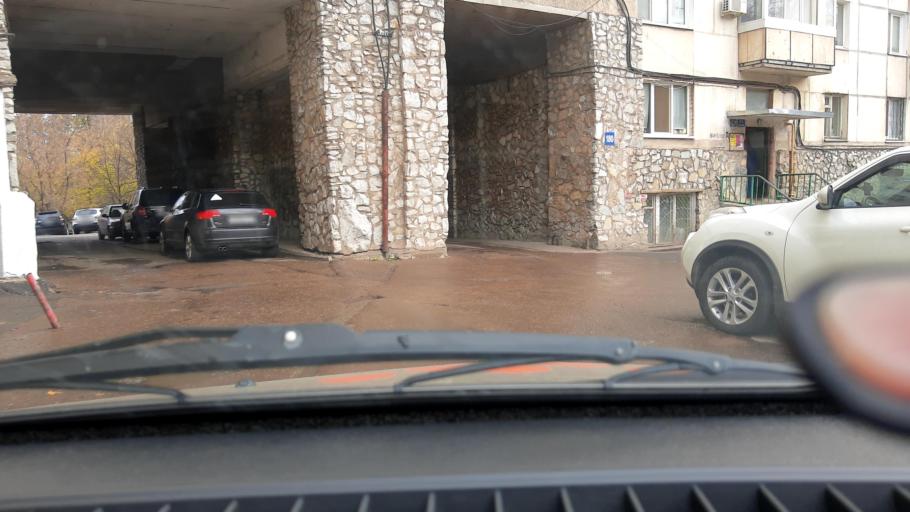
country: RU
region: Bashkortostan
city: Ufa
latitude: 54.7948
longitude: 56.0403
